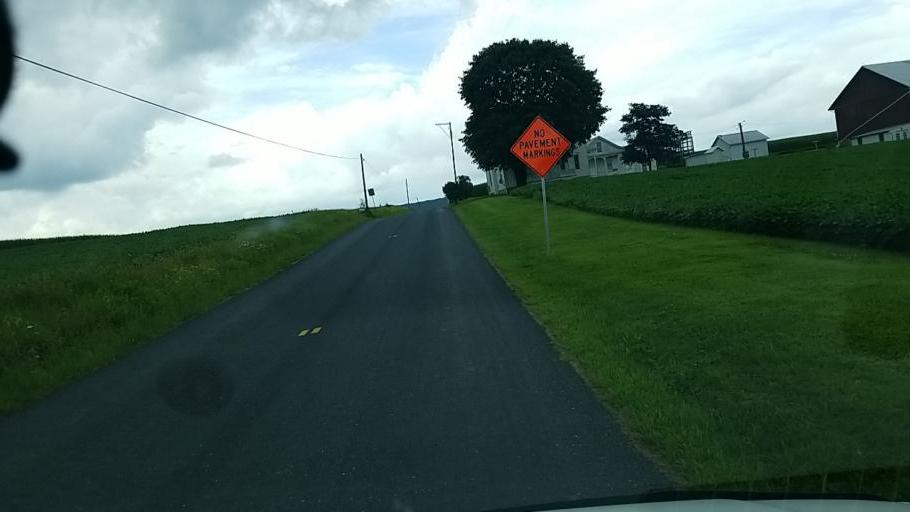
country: US
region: Pennsylvania
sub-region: Dauphin County
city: Elizabethville
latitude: 40.5795
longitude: -76.8495
